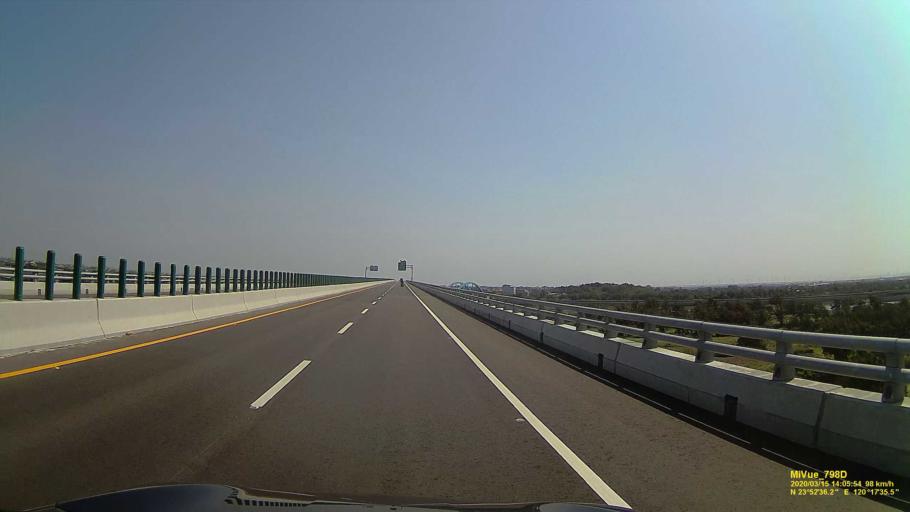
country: TW
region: Taiwan
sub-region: Yunlin
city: Douliu
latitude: 23.8761
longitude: 120.2933
